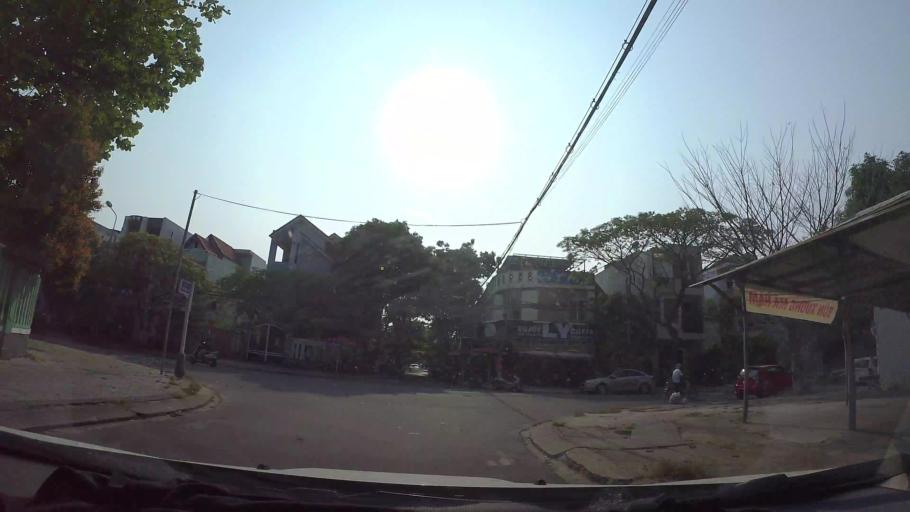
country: VN
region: Da Nang
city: Cam Le
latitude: 16.0226
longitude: 108.2064
